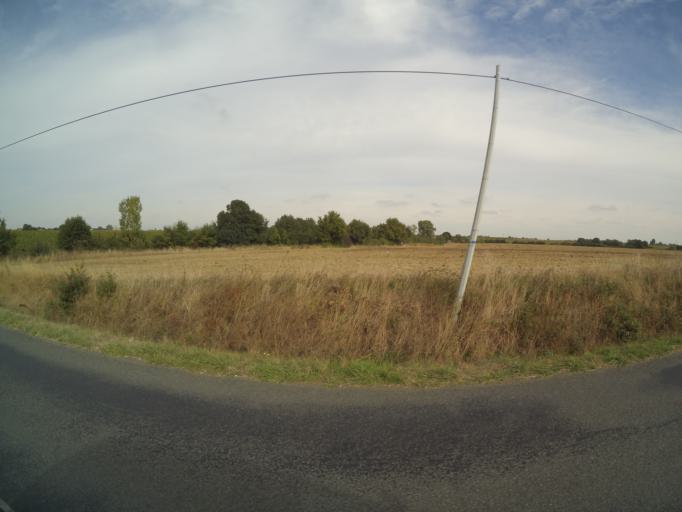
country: FR
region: Pays de la Loire
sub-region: Departement de Maine-et-Loire
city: Martigne-Briand
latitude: 47.2082
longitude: -0.4786
